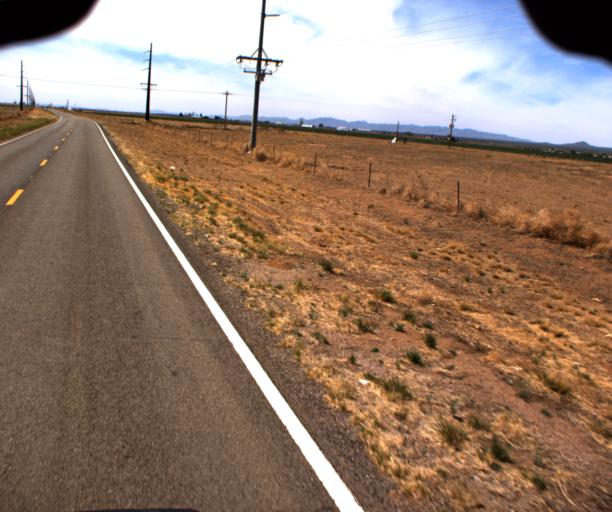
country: US
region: Arizona
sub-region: Cochise County
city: Tombstone
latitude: 31.8199
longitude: -109.6951
